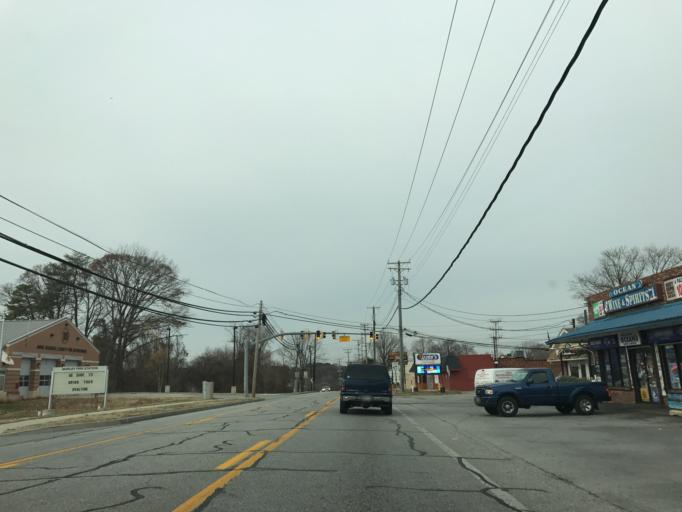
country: US
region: Maryland
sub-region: Anne Arundel County
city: Glen Burnie
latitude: 39.1522
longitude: -76.5957
